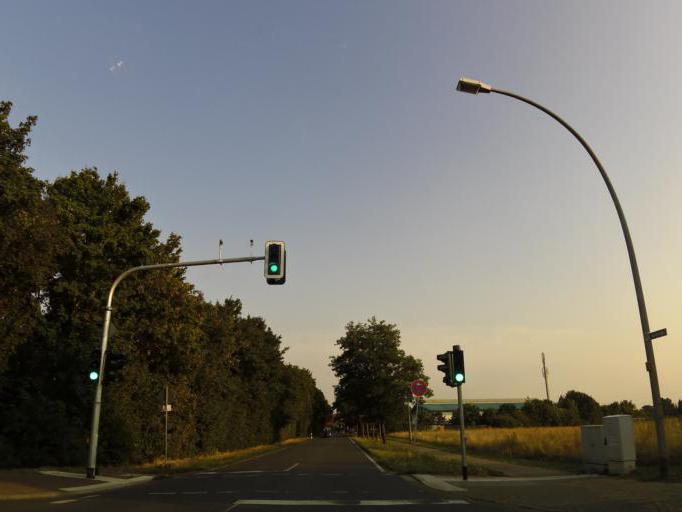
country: DE
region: Hesse
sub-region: Regierungsbezirk Darmstadt
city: Buttelborn
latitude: 49.9309
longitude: 8.5443
